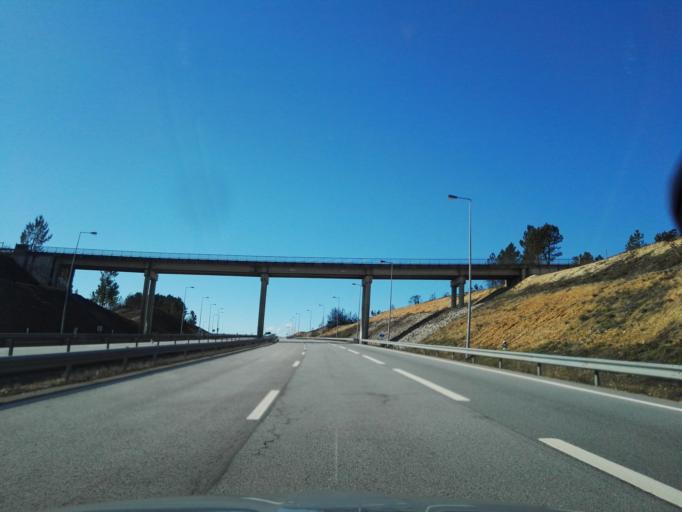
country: PT
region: Santarem
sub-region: Macao
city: Macao
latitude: 39.5175
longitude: -8.0067
